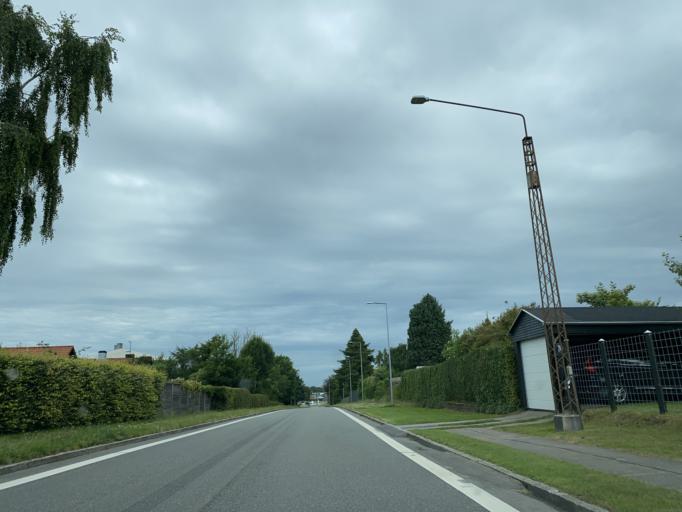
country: DK
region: South Denmark
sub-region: Sonderborg Kommune
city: Sonderborg
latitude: 54.9208
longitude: 9.7985
